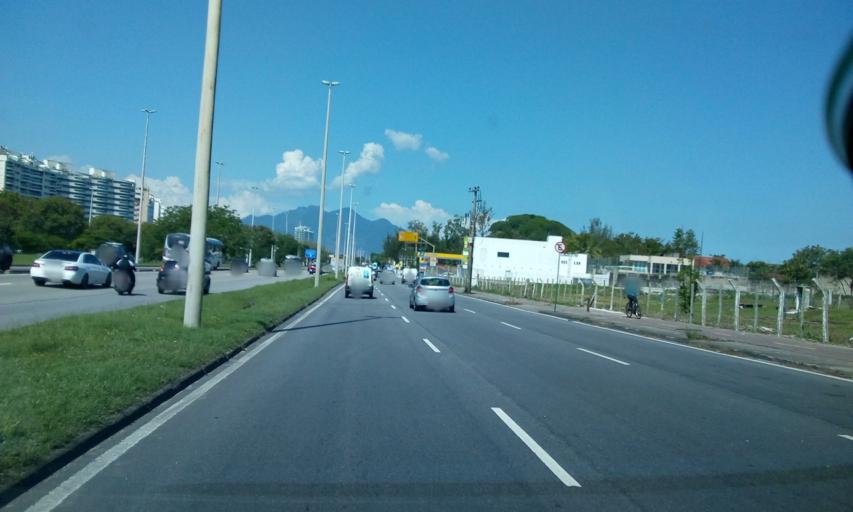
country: BR
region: Rio de Janeiro
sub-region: Nilopolis
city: Nilopolis
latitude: -23.0048
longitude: -43.4287
